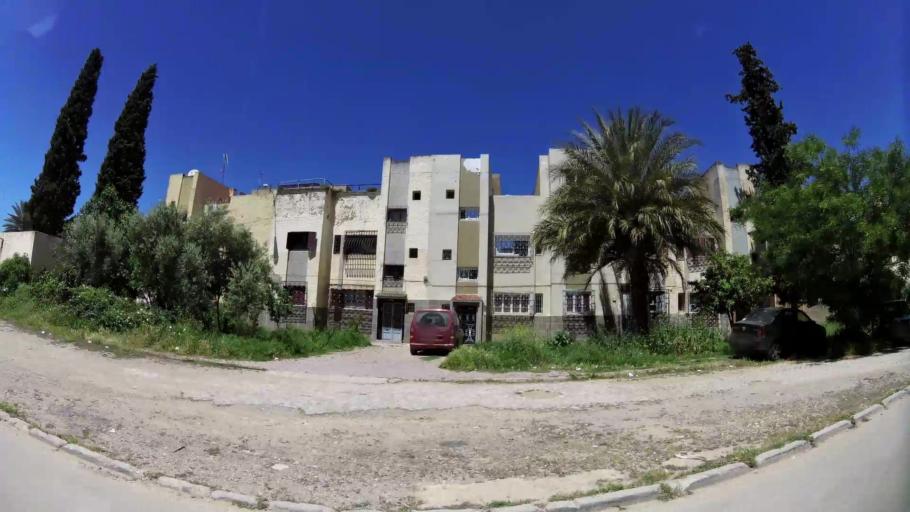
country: MA
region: Meknes-Tafilalet
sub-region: Meknes
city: Meknes
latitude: 33.8789
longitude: -5.5679
